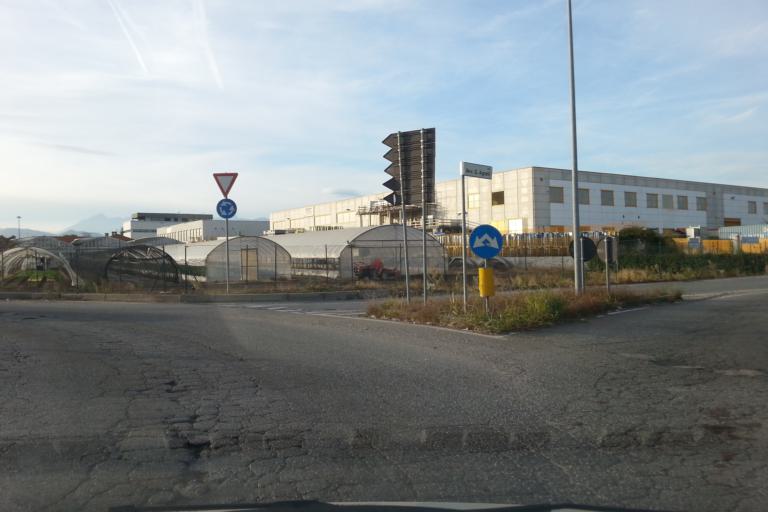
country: IT
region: Piedmont
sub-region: Provincia di Torino
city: Pasta
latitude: 44.9979
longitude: 7.5551
